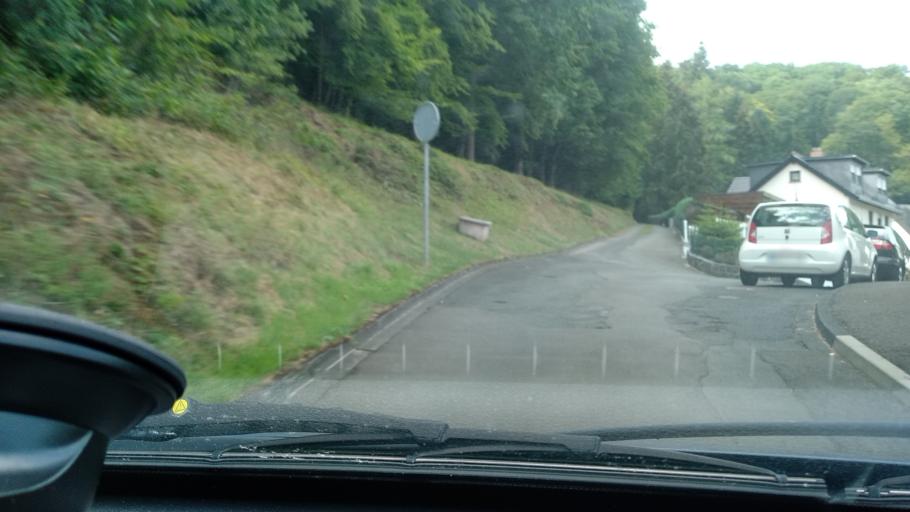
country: DE
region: Hesse
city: Dillenburg
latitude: 50.7412
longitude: 8.2983
